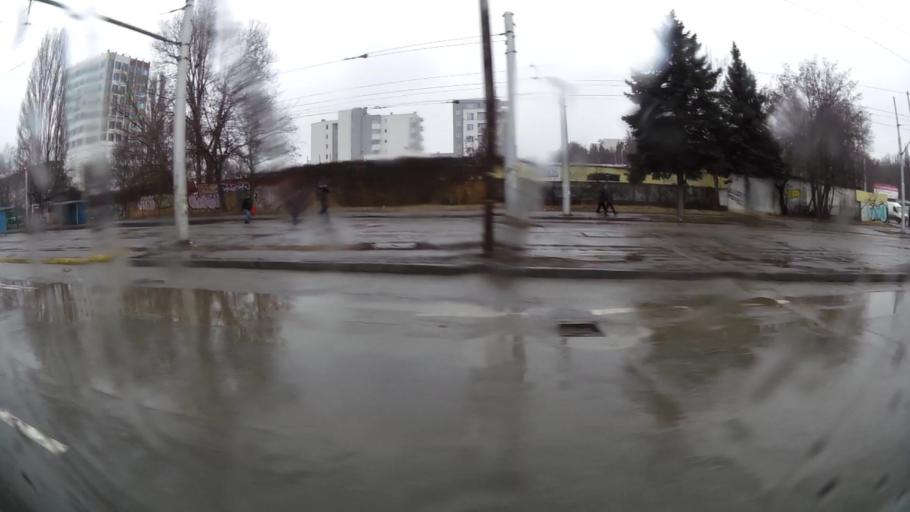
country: BG
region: Sofia-Capital
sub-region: Stolichna Obshtina
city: Sofia
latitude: 42.6738
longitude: 23.3823
